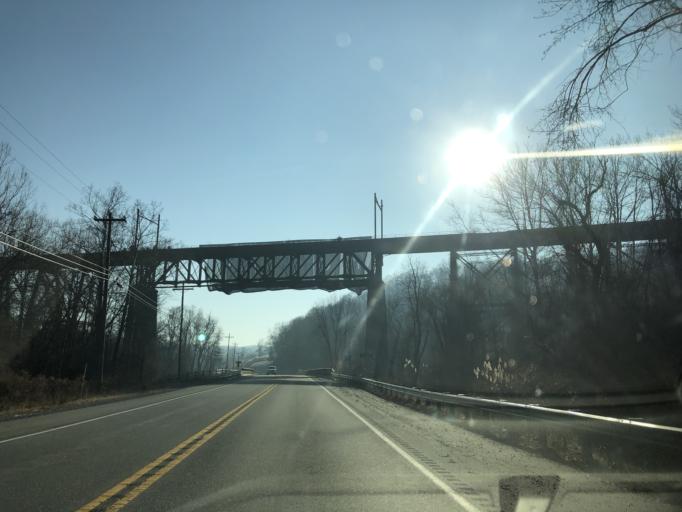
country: US
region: Pennsylvania
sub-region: Chester County
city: Downingtown
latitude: 39.9959
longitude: -75.7006
